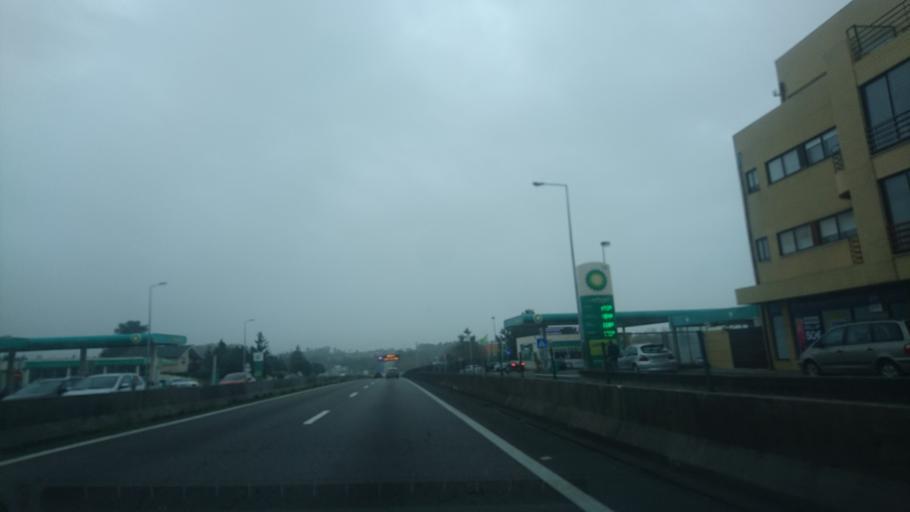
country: PT
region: Porto
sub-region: Vila Nova de Gaia
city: Vilar do Paraiso
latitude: 41.0943
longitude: -8.6292
